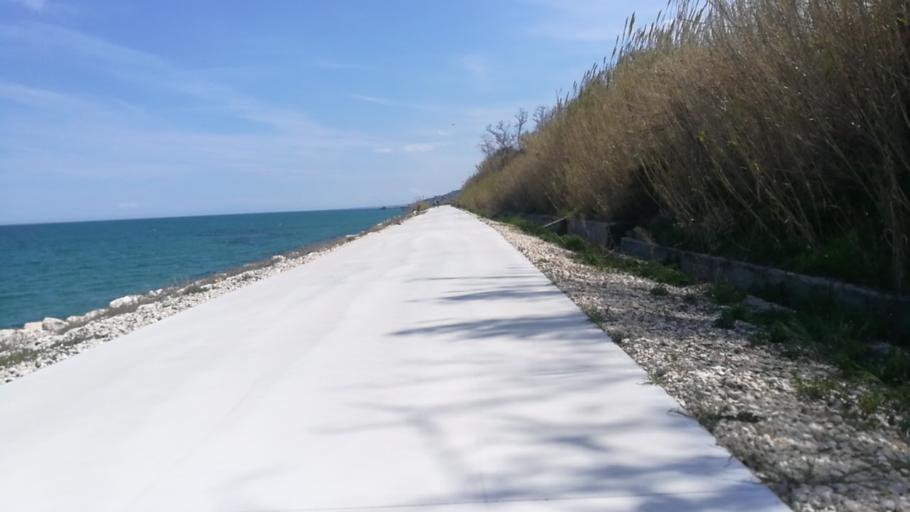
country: IT
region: Abruzzo
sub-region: Provincia di Chieti
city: Marina di San Vito
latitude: 42.3240
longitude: 14.4275
